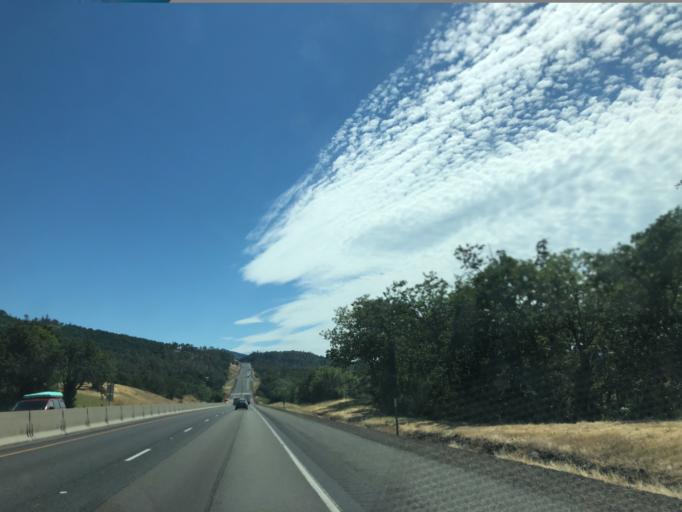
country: US
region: Oregon
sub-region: Douglas County
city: Sutherlin
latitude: 43.4205
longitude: -123.3221
